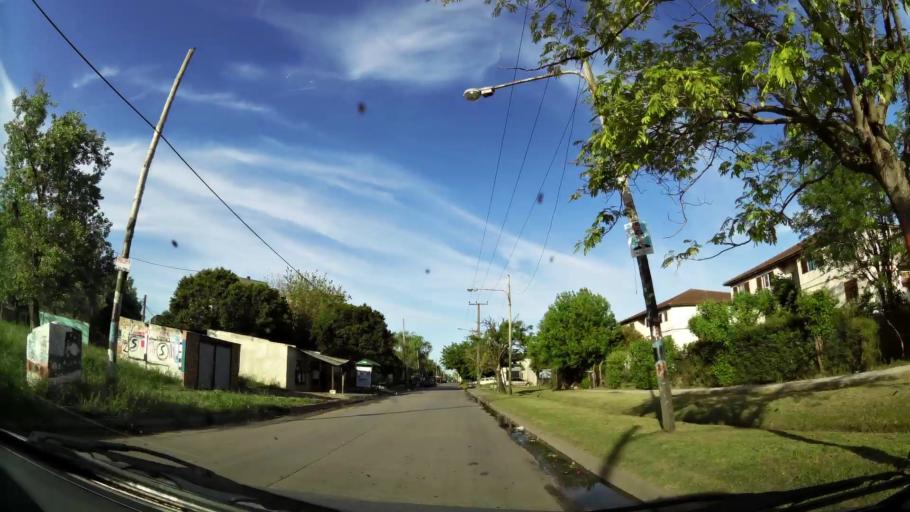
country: AR
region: Buenos Aires
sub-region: Partido de Almirante Brown
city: Adrogue
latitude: -34.8171
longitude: -58.3333
